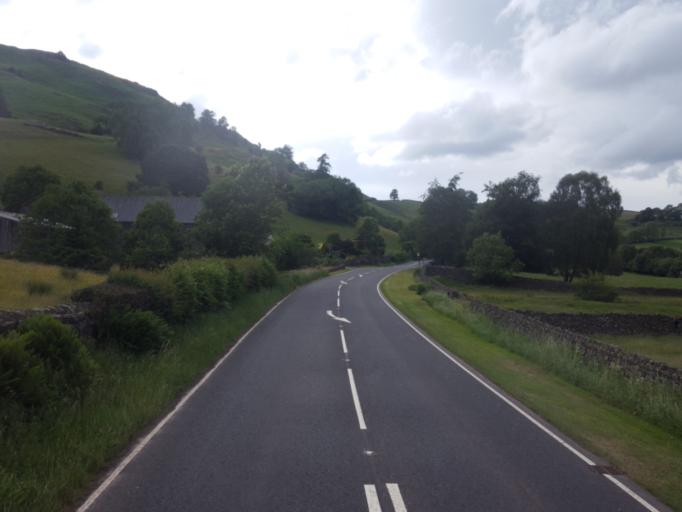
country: GB
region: England
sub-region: Cumbria
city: Keswick
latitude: 54.5861
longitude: -3.0930
